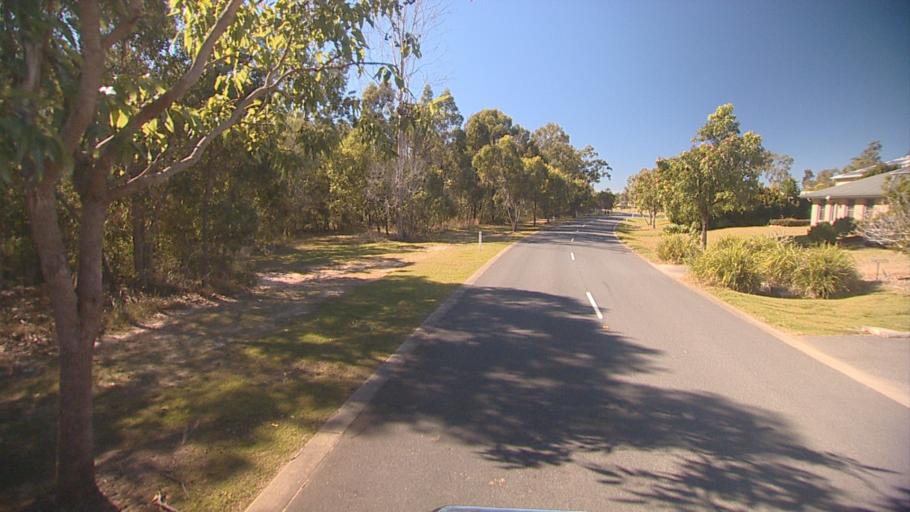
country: AU
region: Queensland
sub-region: Logan
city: North Maclean
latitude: -27.7515
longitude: 152.9598
